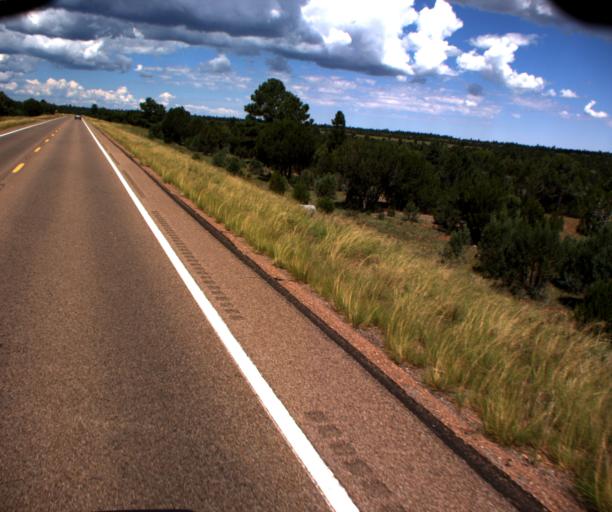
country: US
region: Arizona
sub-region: Navajo County
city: Heber-Overgaard
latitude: 34.3886
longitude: -110.5029
